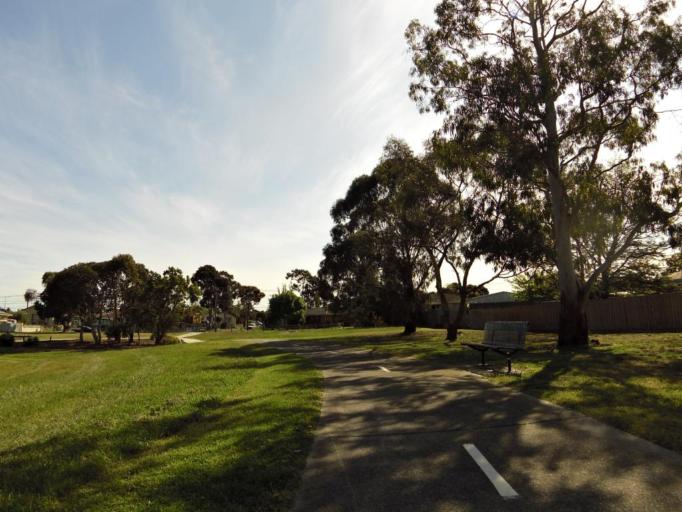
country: AU
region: Victoria
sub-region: Brimbank
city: Sunshine West
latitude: -37.7975
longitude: 144.8205
